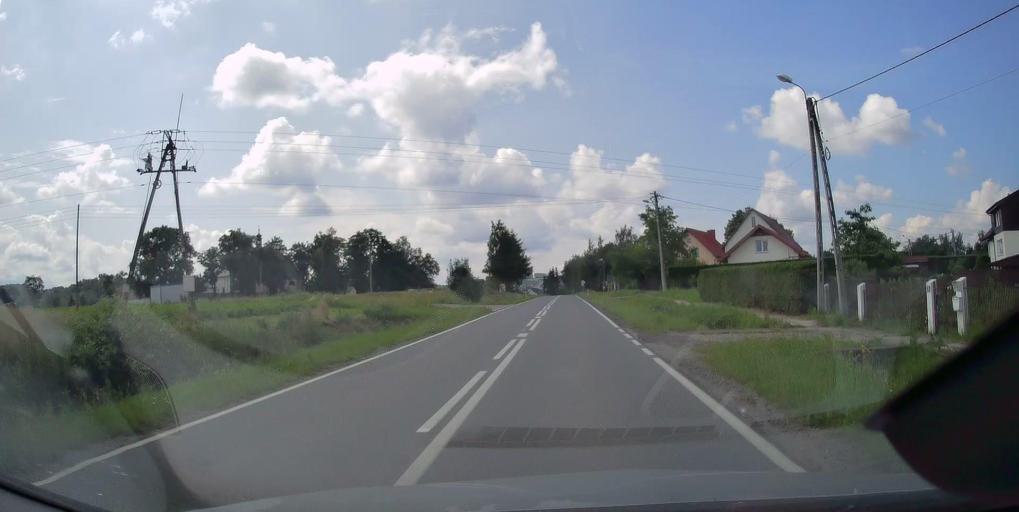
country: PL
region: Lesser Poland Voivodeship
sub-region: Powiat tarnowski
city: Zakliczyn
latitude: 49.8515
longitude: 20.8108
